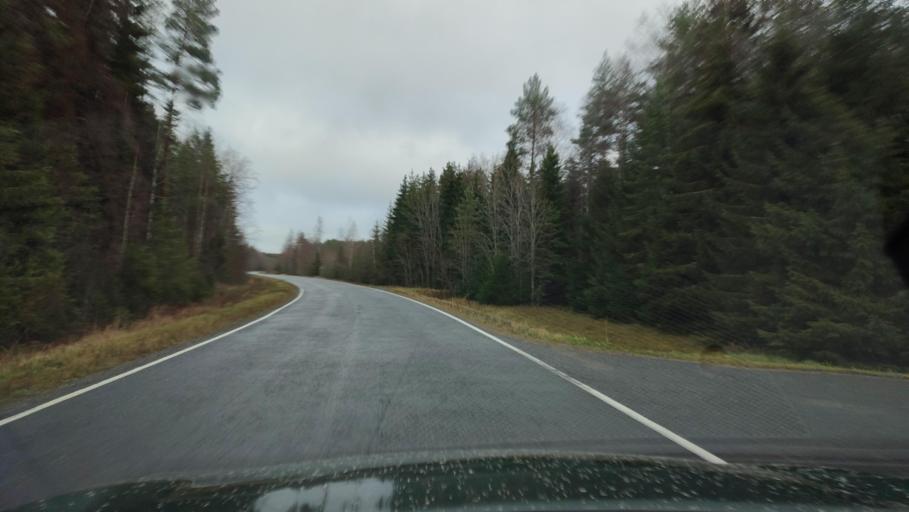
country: FI
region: Ostrobothnia
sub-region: Sydosterbotten
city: Kristinestad
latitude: 62.3428
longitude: 21.5273
